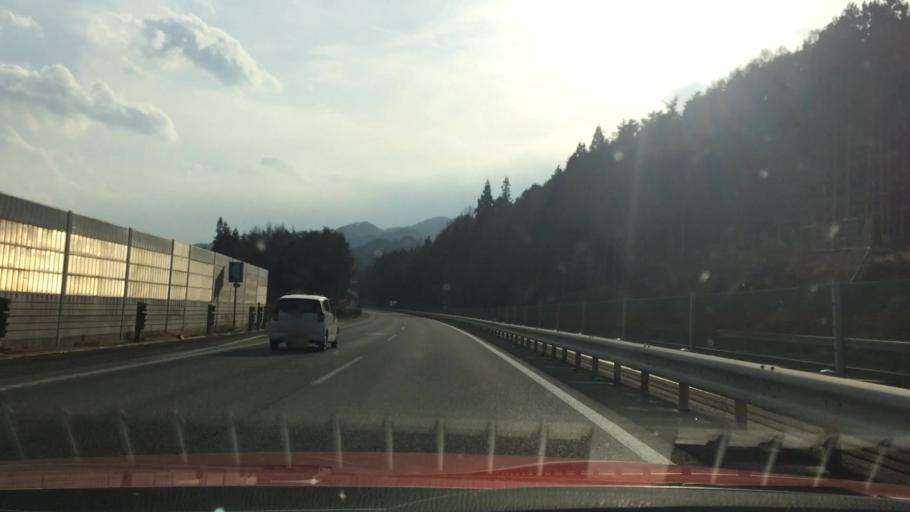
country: JP
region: Nagano
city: Ina
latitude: 35.8210
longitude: 137.9269
